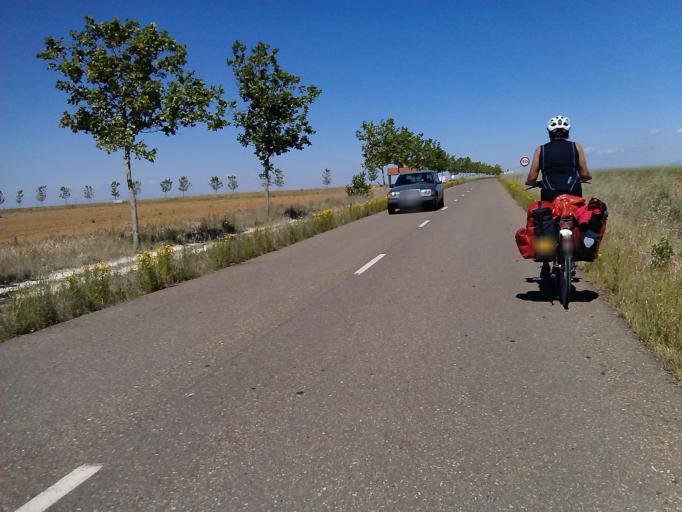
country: ES
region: Castille and Leon
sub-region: Provincia de Leon
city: Villamoratiel de las Matas
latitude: 42.4599
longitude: -5.2981
